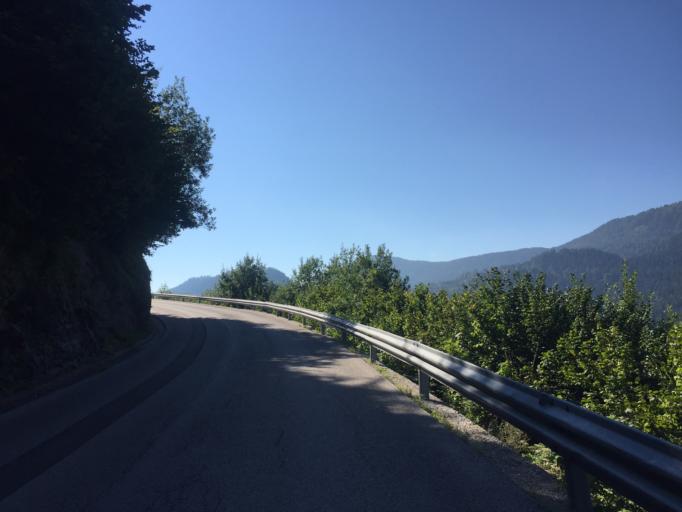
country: IT
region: Friuli Venezia Giulia
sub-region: Provincia di Udine
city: Forni Avoltri
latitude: 46.5769
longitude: 12.8047
